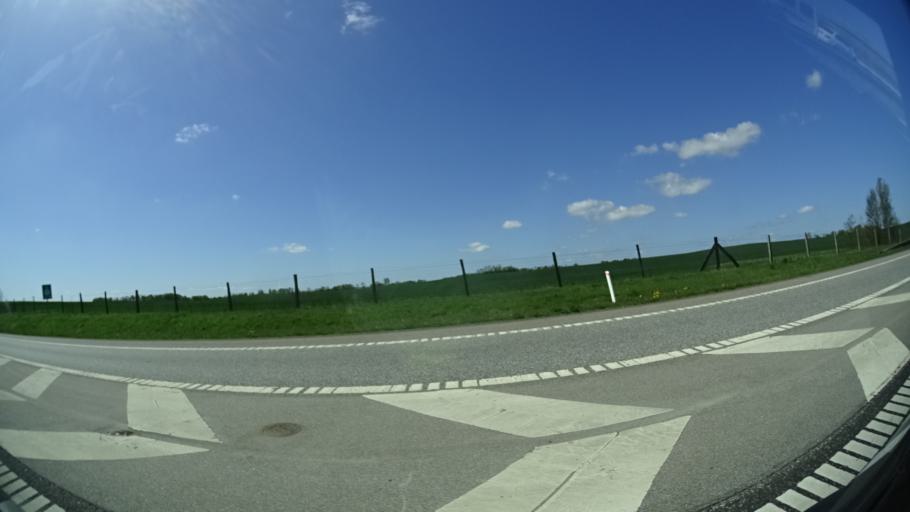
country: DK
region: Central Jutland
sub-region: Arhus Kommune
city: Framlev
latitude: 56.1617
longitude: 10.0465
